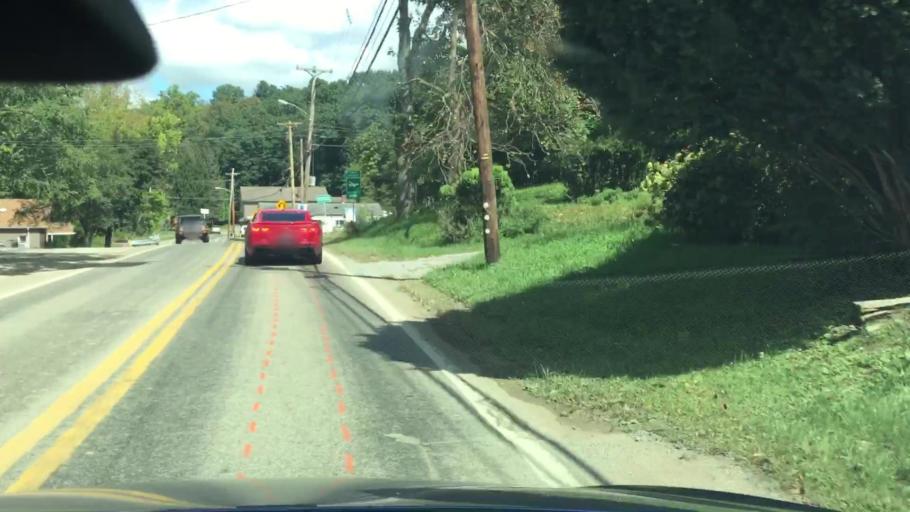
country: US
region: Pennsylvania
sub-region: Allegheny County
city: Russellton
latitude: 40.5889
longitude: -79.8278
